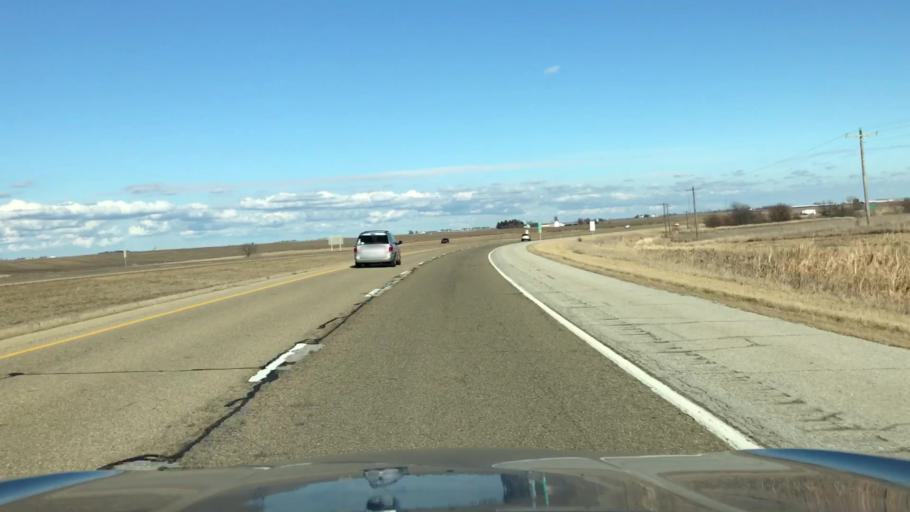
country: US
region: Illinois
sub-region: McLean County
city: Lexington
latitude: 40.6527
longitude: -88.8049
